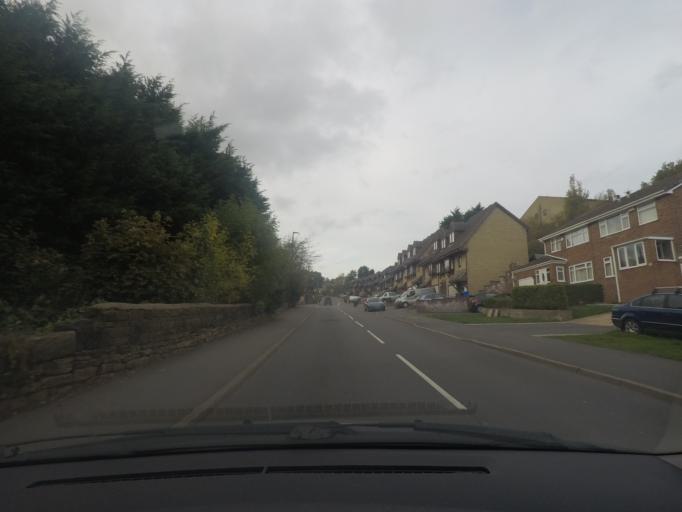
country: GB
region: England
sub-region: Sheffield
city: Oughtibridge
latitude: 53.4206
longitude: -1.4985
